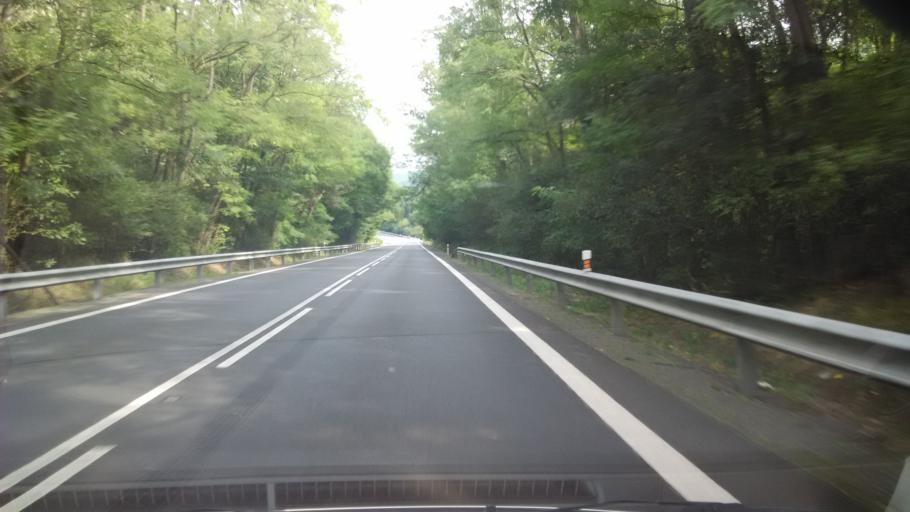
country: SK
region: Banskobystricky
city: Krupina
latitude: 48.3169
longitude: 19.0477
